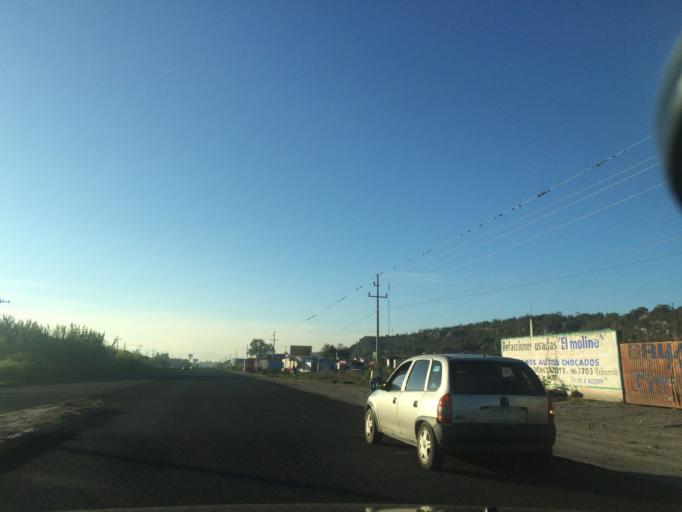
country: MX
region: Puebla
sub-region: Santiago Miahuatlan
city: San Jose Monte Chiquito
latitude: 18.4842
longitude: -97.4510
